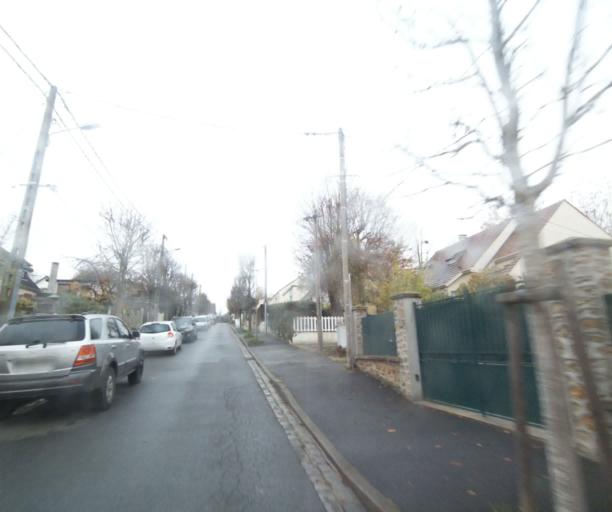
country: FR
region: Ile-de-France
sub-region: Departement de l'Essonne
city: Ris-Orangis
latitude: 48.6481
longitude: 2.4324
